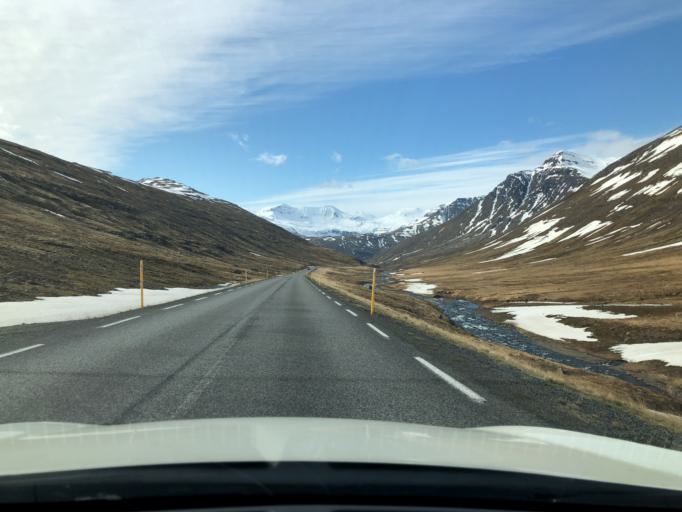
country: IS
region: East
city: Reydarfjoerdur
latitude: 65.0666
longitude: -14.3446
